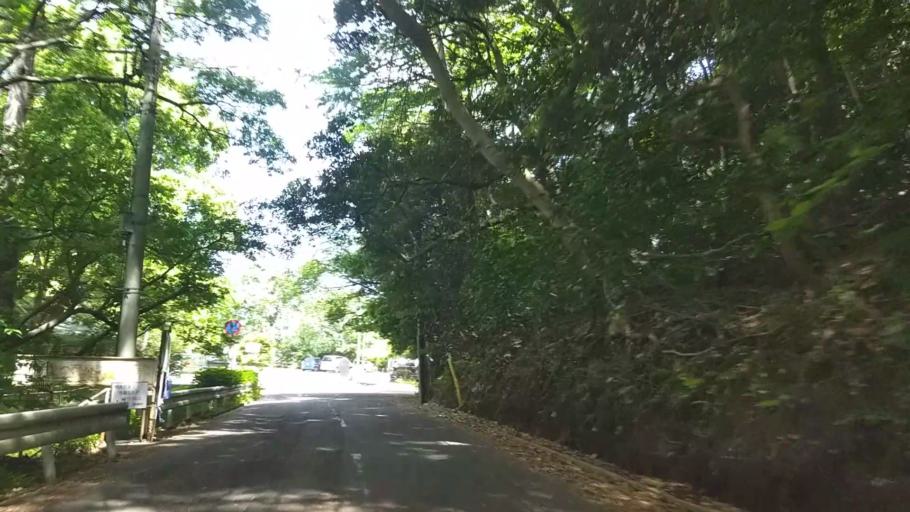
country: JP
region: Kanagawa
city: Yugawara
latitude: 35.1444
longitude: 139.1524
